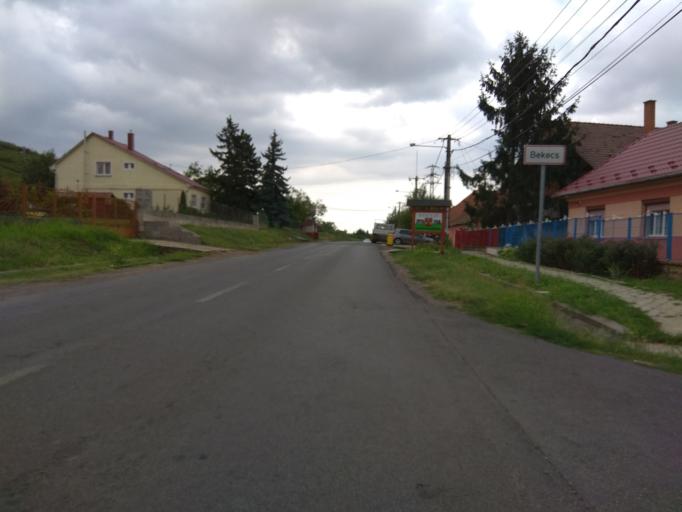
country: HU
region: Borsod-Abauj-Zemplen
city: Bekecs
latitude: 48.1546
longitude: 21.1617
